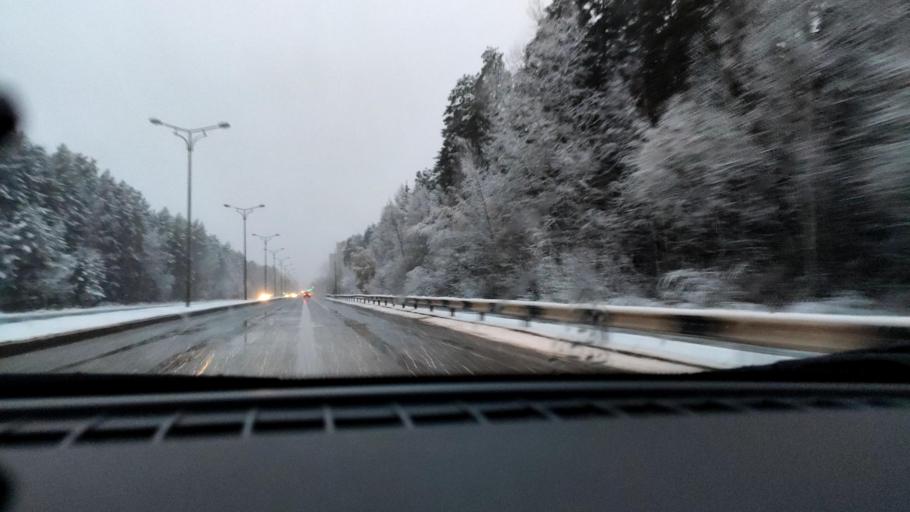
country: RU
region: Perm
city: Kondratovo
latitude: 58.0191
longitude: 55.9886
